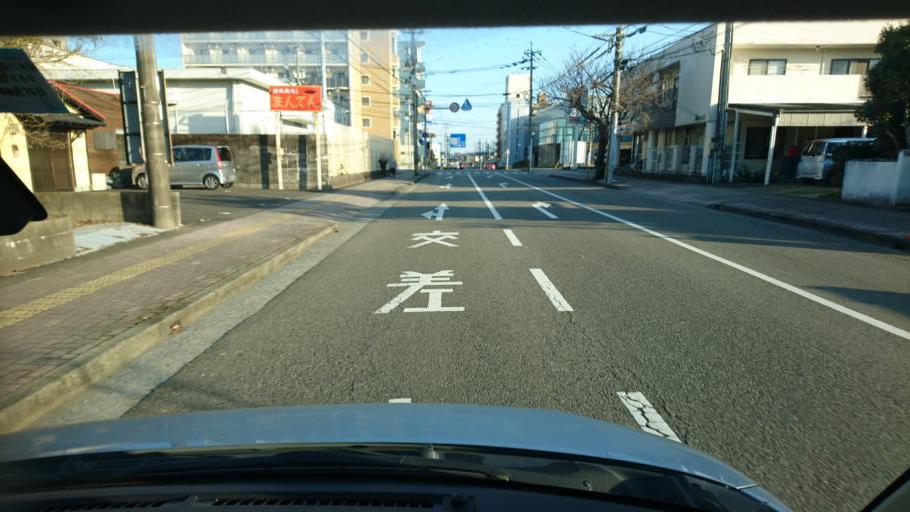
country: JP
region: Miyazaki
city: Miyazaki-shi
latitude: 31.8296
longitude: 131.4200
